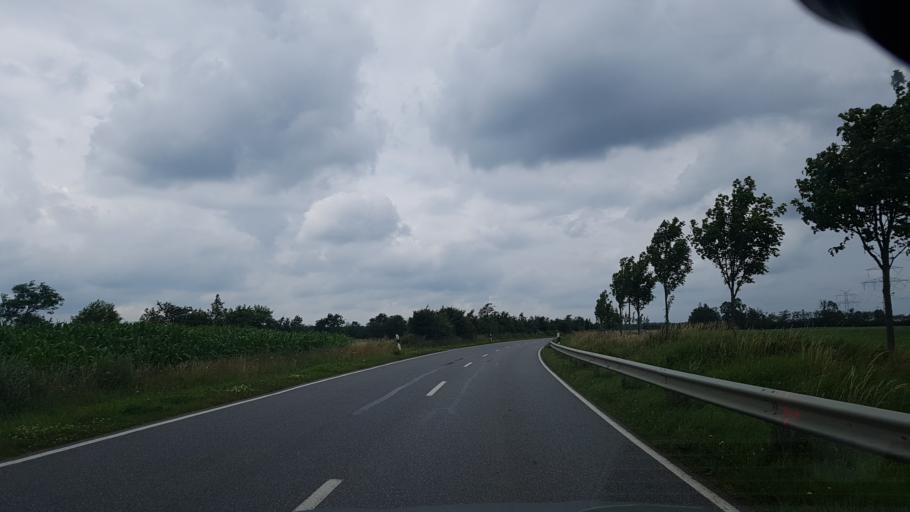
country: DE
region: Schleswig-Holstein
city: Osterby
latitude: 54.8044
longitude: 9.2414
